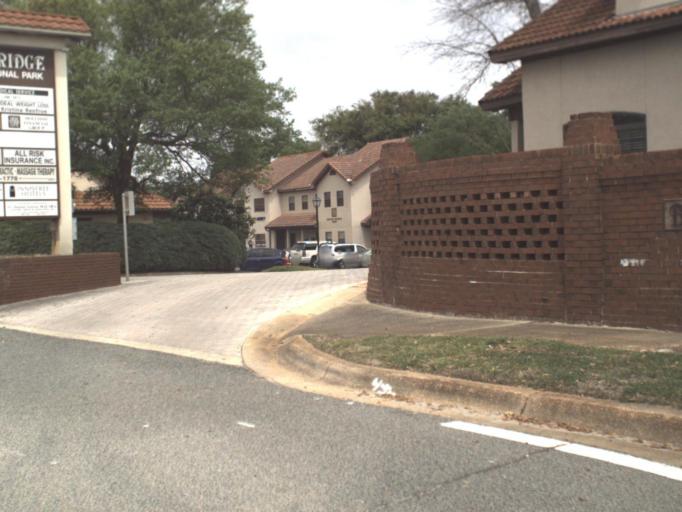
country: US
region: Florida
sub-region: Santa Rosa County
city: Gulf Breeze
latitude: 30.3679
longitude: -87.1724
